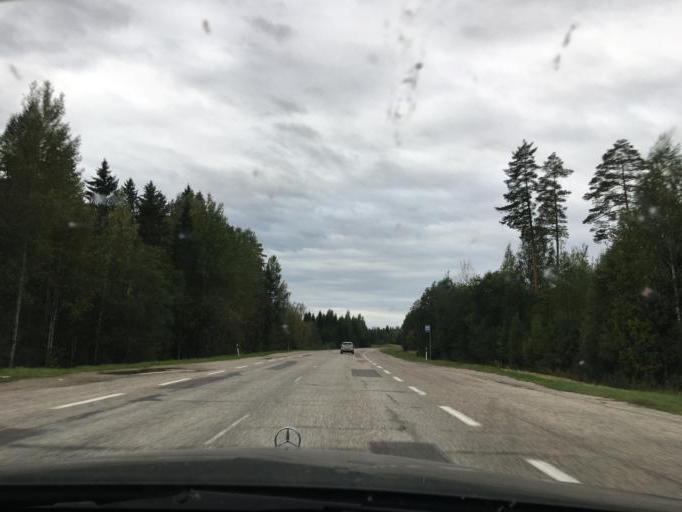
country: LV
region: Aluksnes Rajons
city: Aluksne
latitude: 57.5882
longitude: 27.0770
